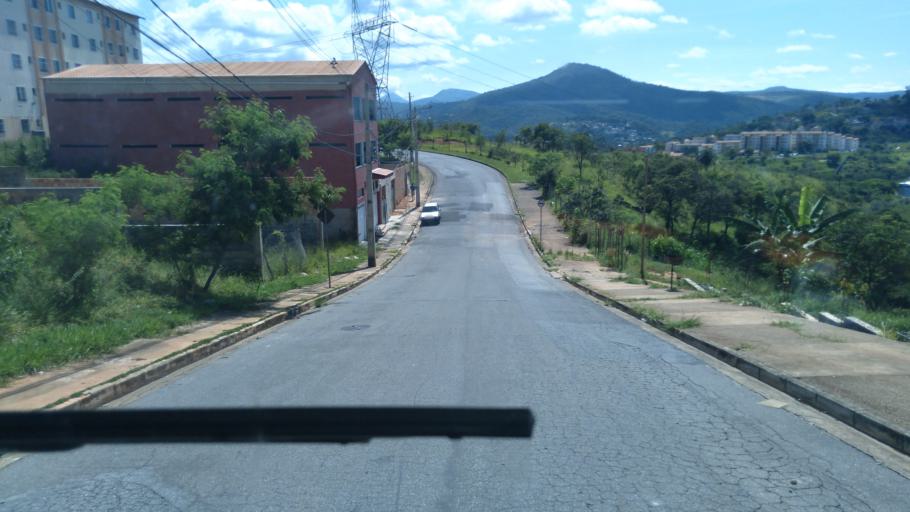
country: BR
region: Minas Gerais
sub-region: Santa Luzia
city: Santa Luzia
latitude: -19.8423
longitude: -43.8833
